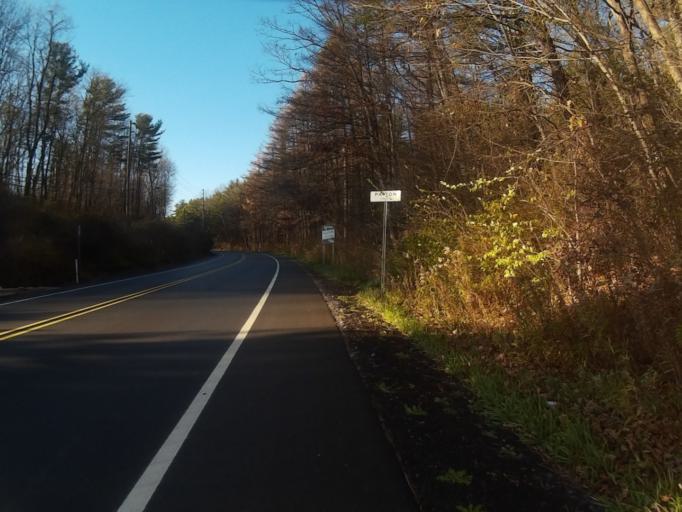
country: US
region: Pennsylvania
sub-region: Centre County
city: State College
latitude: 40.8251
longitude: -77.8696
